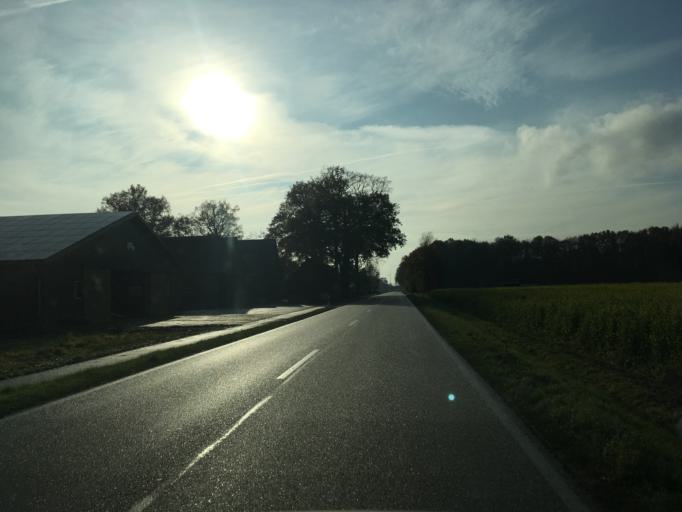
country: DE
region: North Rhine-Westphalia
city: Stadtlohn
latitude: 52.0129
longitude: 6.9430
